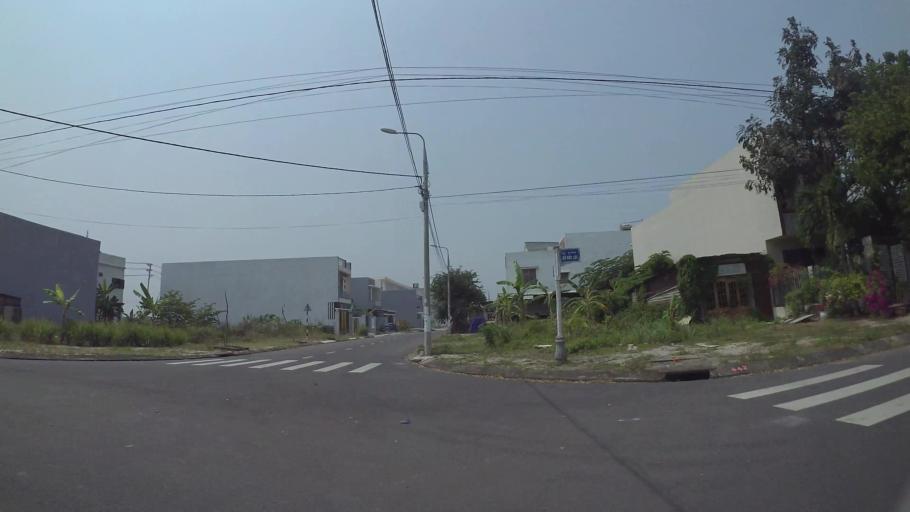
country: VN
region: Da Nang
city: Cam Le
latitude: 15.9998
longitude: 108.2204
